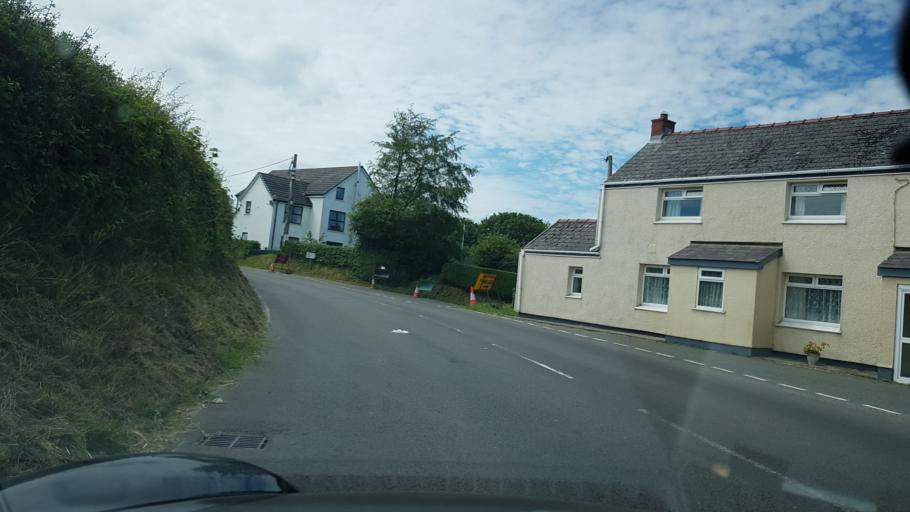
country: GB
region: Wales
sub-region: Carmarthenshire
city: Whitland
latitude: 51.7835
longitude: -4.6355
